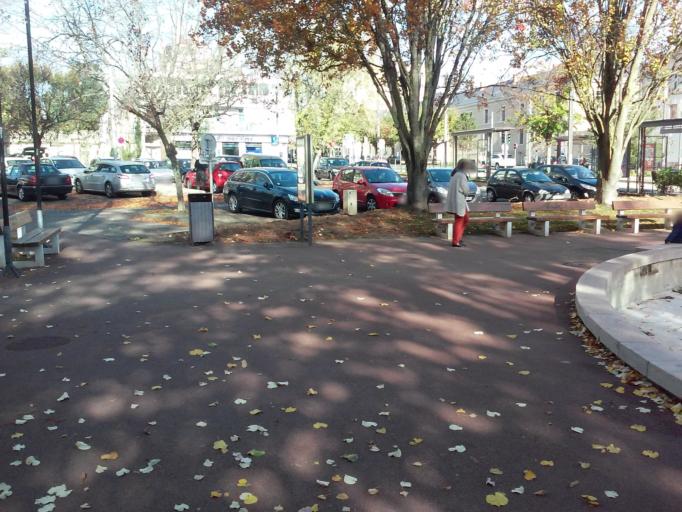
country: FR
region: Pays de la Loire
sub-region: Departement de la Vendee
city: La Roche-sur-Yon
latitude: 46.6693
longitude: -1.4321
